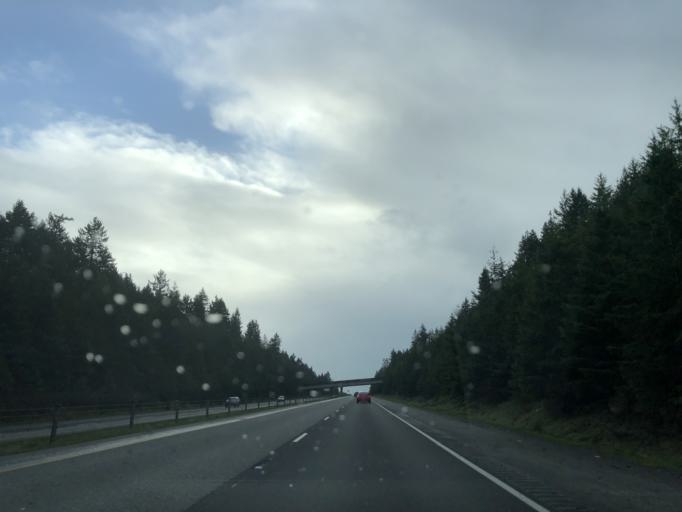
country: US
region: Washington
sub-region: Kitsap County
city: Poulsbo
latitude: 47.7307
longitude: -122.6761
